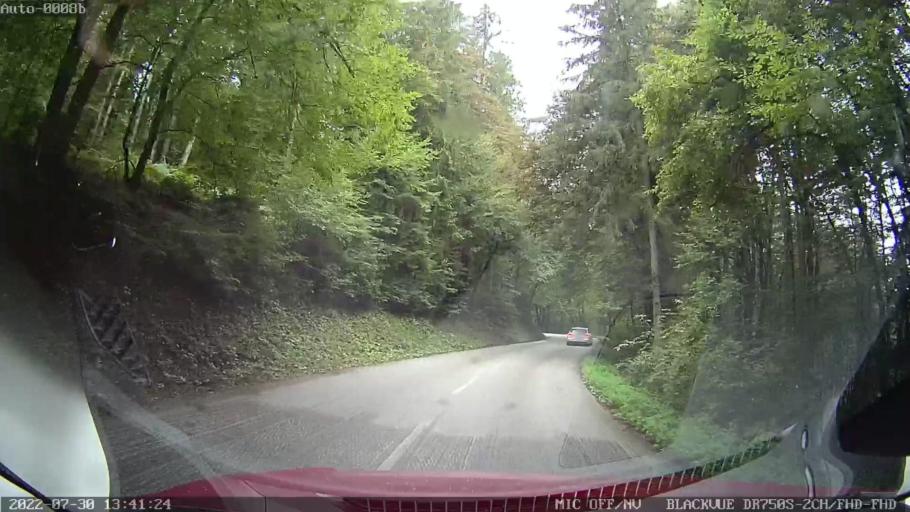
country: SI
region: Ivancna Gorica
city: Sentvid pri Sticni
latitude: 45.9023
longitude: 14.8980
